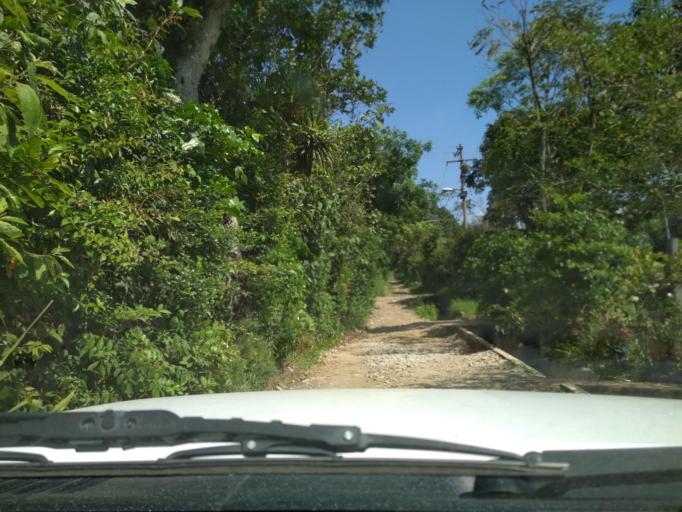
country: MX
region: Veracruz
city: Cordoba
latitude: 18.8724
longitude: -96.9092
